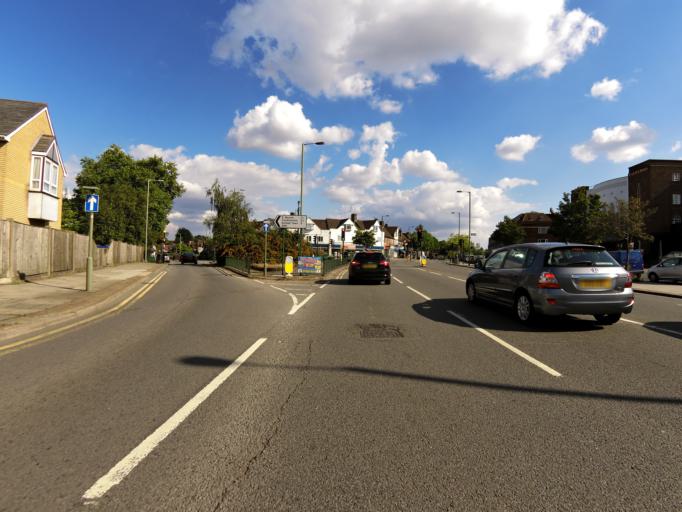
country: GB
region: England
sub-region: Greater London
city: Barnet
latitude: 51.6470
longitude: -0.1879
